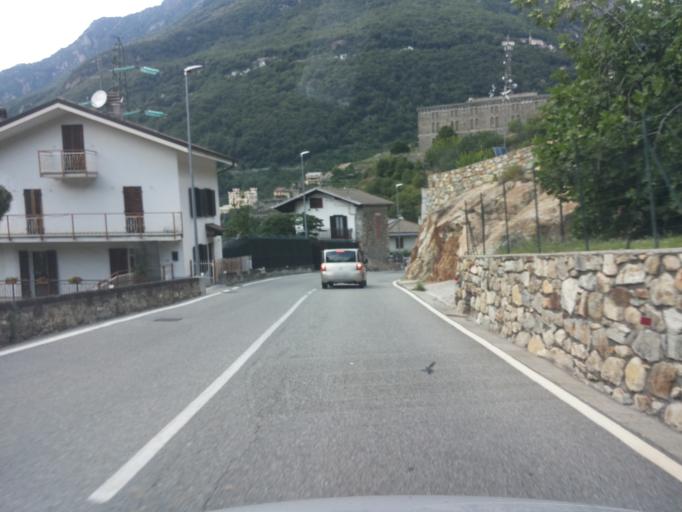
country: IT
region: Aosta Valley
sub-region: Valle d'Aosta
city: Pont-Saint-Martin
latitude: 45.5960
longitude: 7.8019
